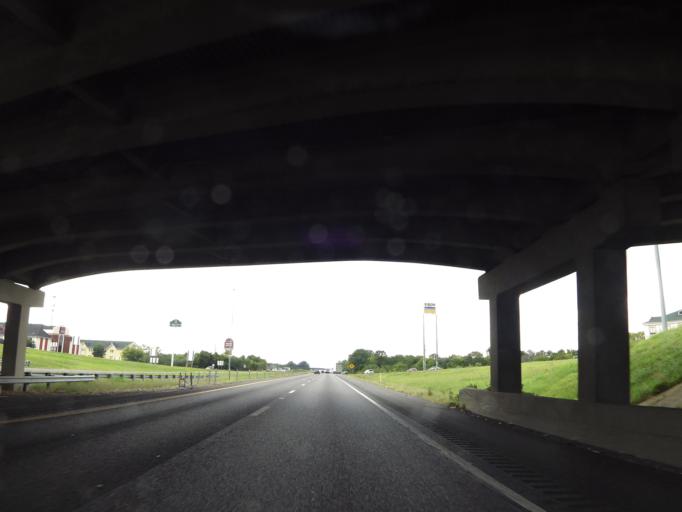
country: US
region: Tennessee
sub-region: Wilson County
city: Lebanon
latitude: 36.1823
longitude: -86.2988
